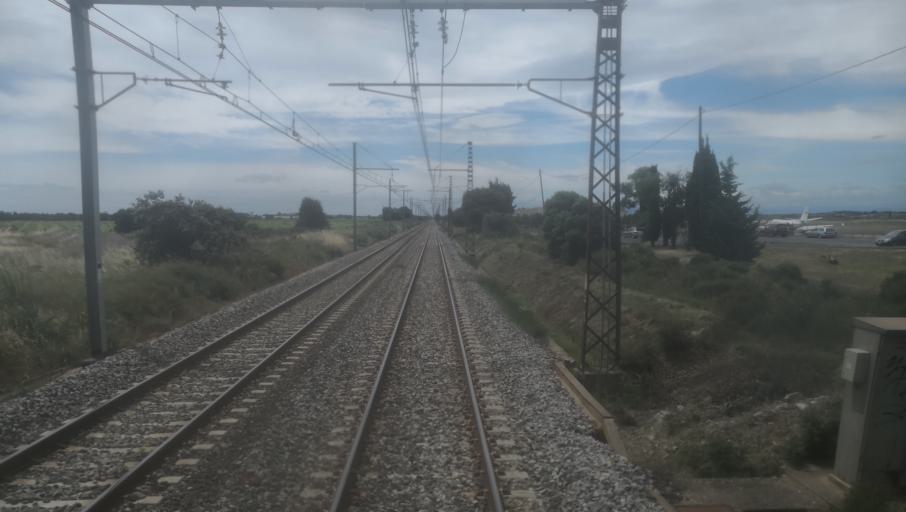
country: FR
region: Languedoc-Roussillon
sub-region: Departement de l'Herault
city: Portiragnes
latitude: 43.3199
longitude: 3.3594
